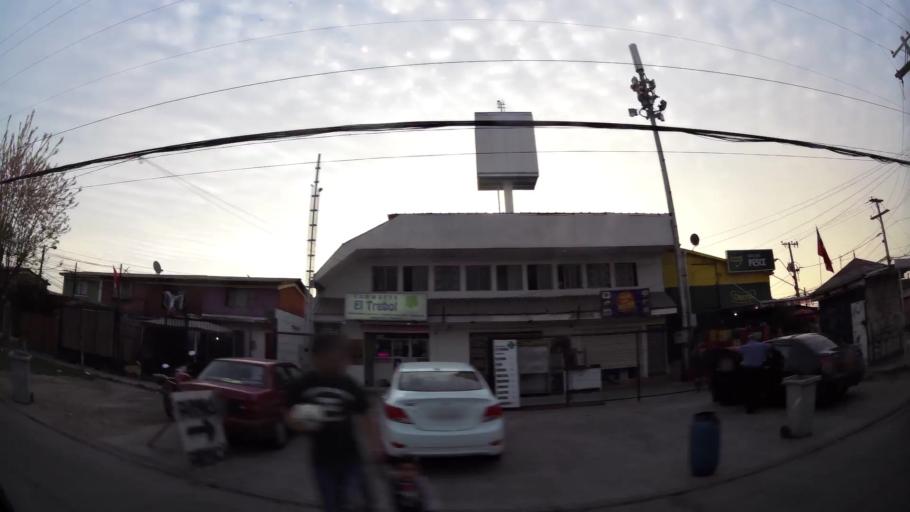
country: CL
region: Santiago Metropolitan
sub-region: Provincia de Santiago
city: Lo Prado
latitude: -33.5158
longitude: -70.7792
